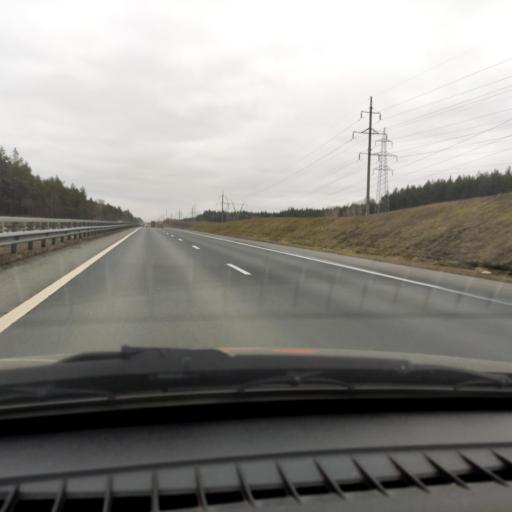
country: RU
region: Samara
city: Povolzhskiy
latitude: 53.5171
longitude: 49.7306
